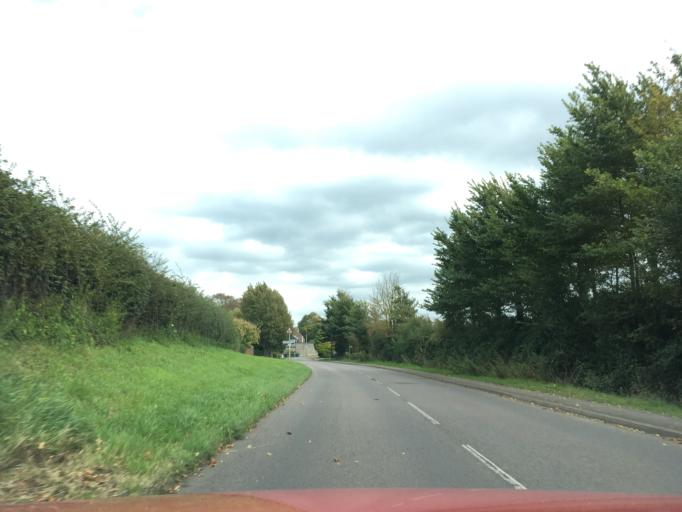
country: GB
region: England
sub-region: South Gloucestershire
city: Almondsbury
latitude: 51.5772
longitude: -2.5722
